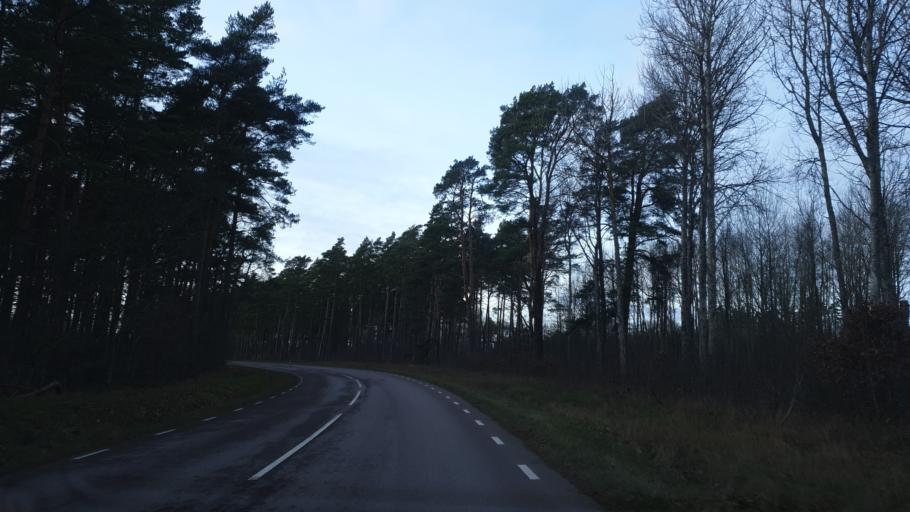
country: SE
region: Kalmar
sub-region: Torsas Kommun
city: Torsas
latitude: 56.2542
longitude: 16.0157
